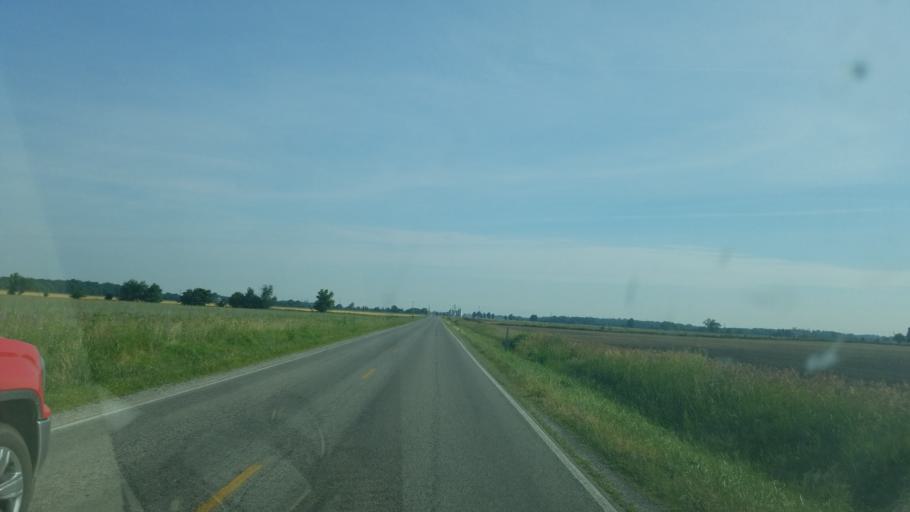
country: US
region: Ohio
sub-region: Hancock County
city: Arlington
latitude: 40.9594
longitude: -83.6985
